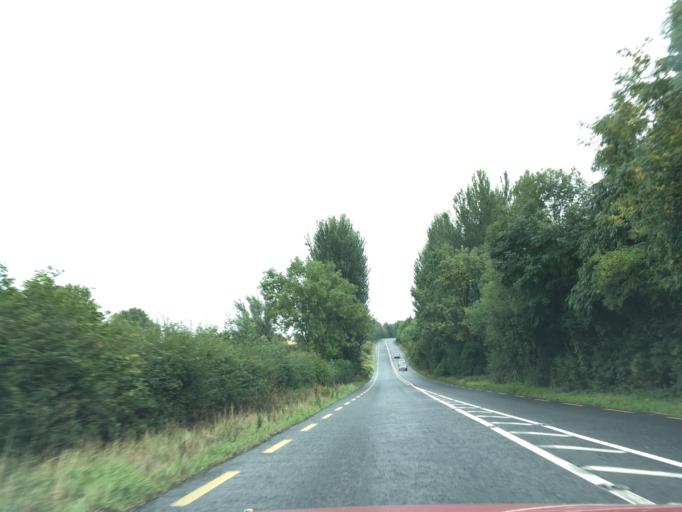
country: IE
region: Munster
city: Carrick-on-Suir
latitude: 52.3652
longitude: -7.5133
